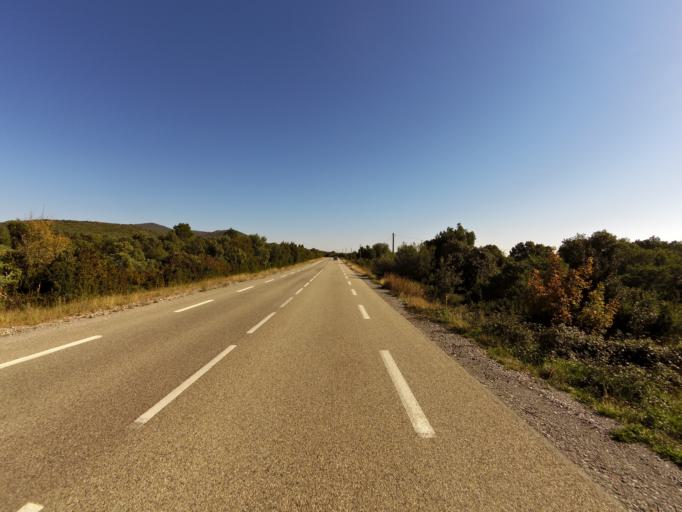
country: FR
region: Rhone-Alpes
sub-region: Departement de l'Ardeche
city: Ruoms
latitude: 44.4017
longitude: 4.4516
